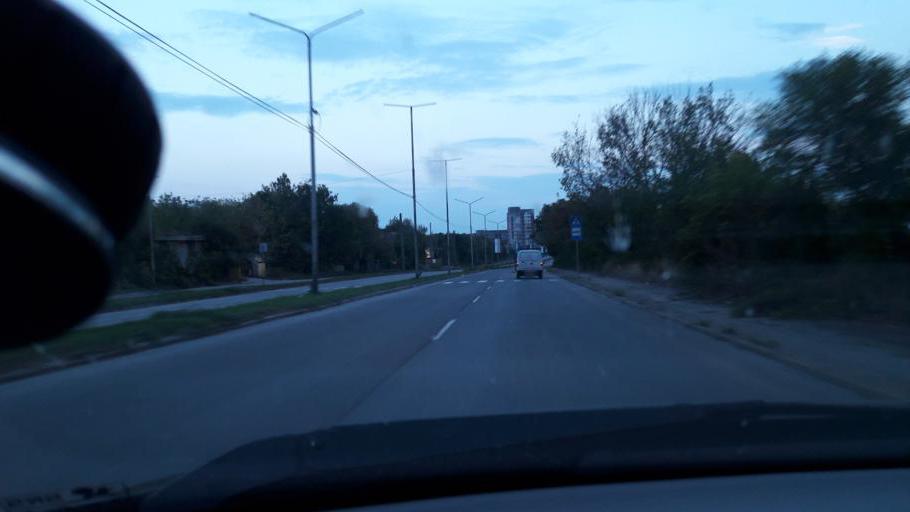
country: BG
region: Razgrad
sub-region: Obshtina Razgrad
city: Razgrad
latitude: 43.5381
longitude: 26.5188
